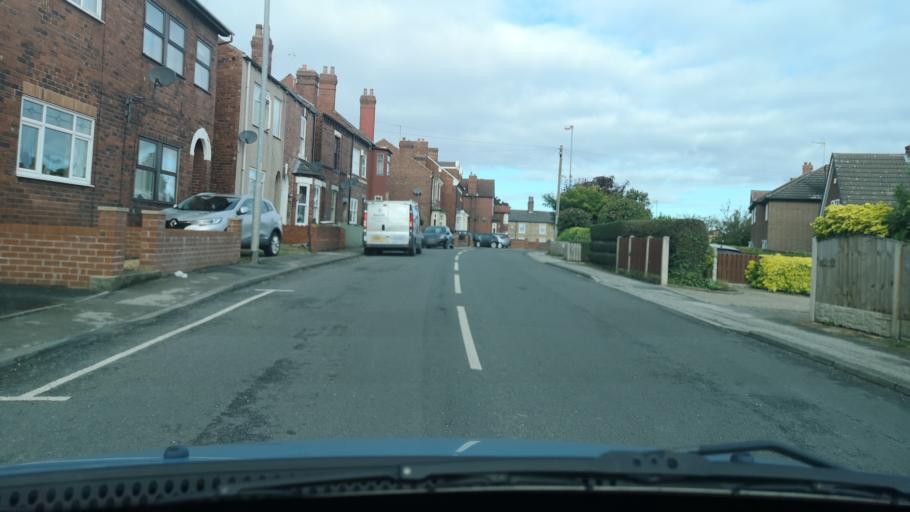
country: GB
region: England
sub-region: City and Borough of Wakefield
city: Normanton
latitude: 53.7054
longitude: -1.4366
